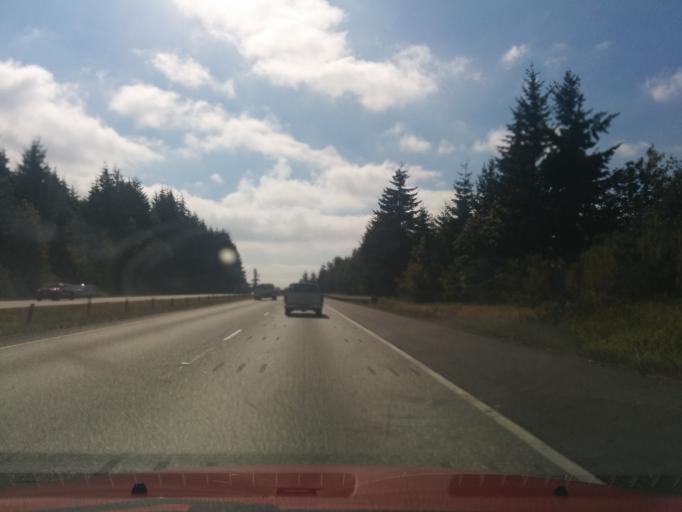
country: US
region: Washington
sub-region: Whatcom County
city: Bellingham
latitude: 48.7313
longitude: -122.4698
